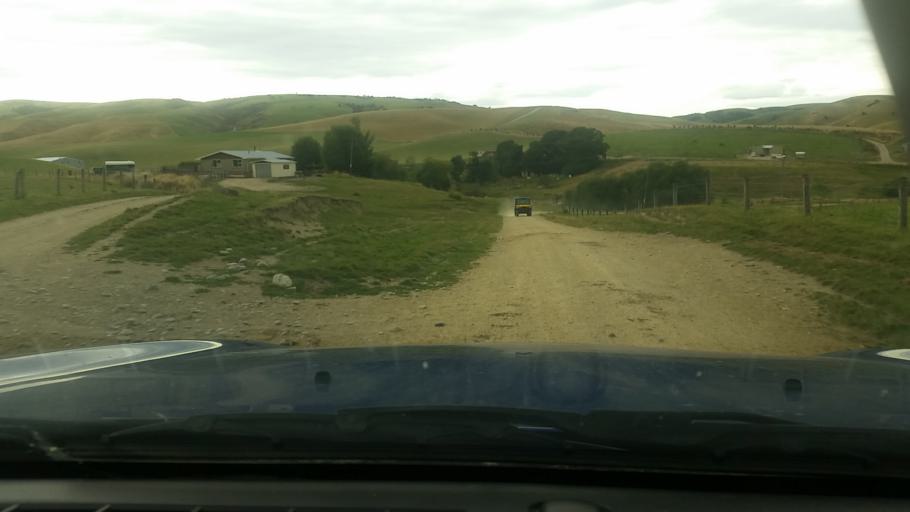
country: NZ
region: Otago
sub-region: Clutha District
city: Balclutha
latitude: -45.7371
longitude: 169.5409
